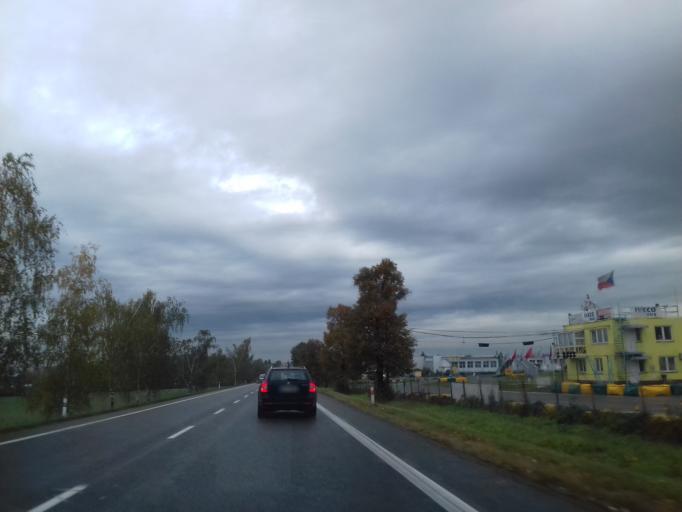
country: CZ
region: Pardubicky
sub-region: Okres Pardubice
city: Vysoke Myto
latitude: 49.9384
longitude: 16.1692
